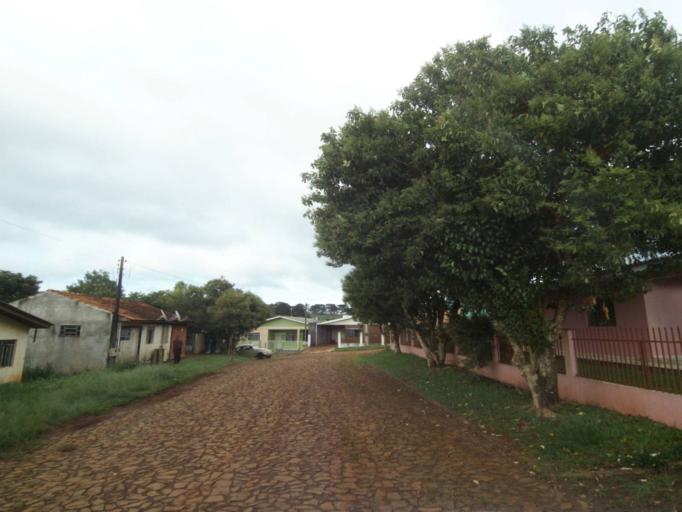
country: BR
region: Parana
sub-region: Pitanga
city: Pitanga
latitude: -24.9418
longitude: -51.8704
